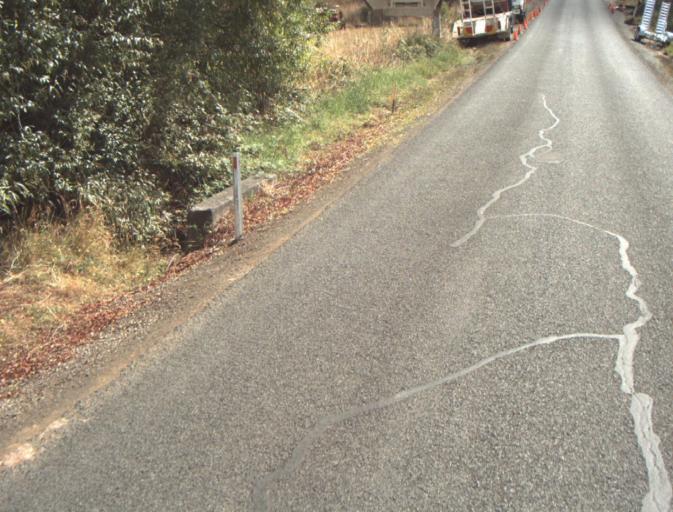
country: AU
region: Tasmania
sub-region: Launceston
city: Mayfield
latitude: -41.2591
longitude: 147.1803
